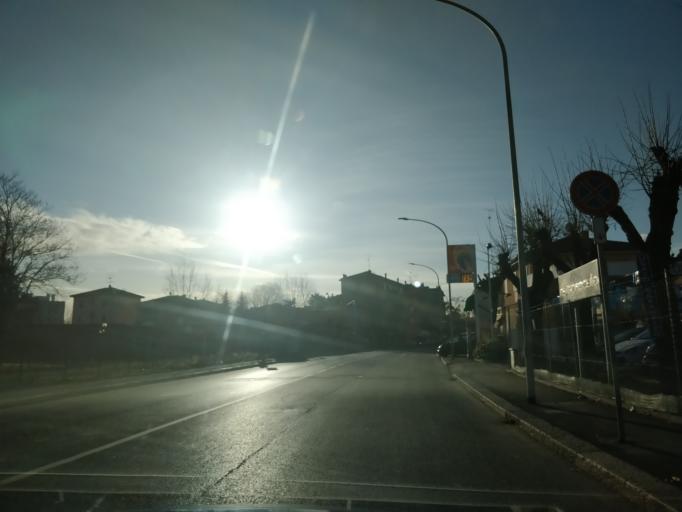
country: IT
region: Emilia-Romagna
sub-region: Provincia di Bologna
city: Bologna
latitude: 44.5177
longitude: 11.3244
